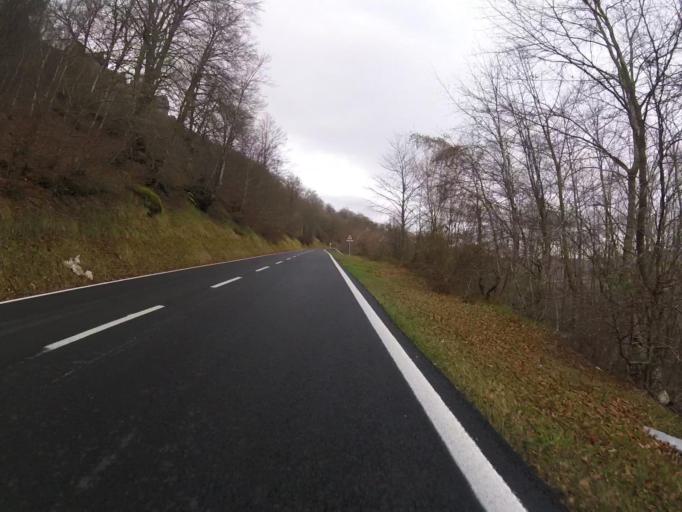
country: ES
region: Navarre
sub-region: Provincia de Navarra
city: Arbizu
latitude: 42.8656
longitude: -2.0284
